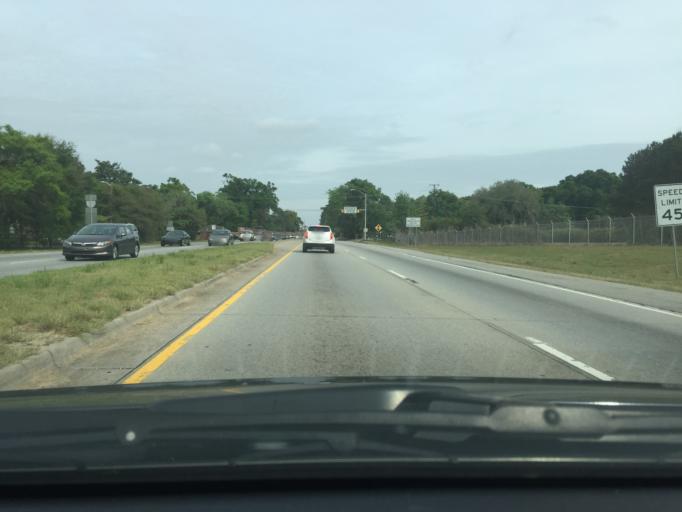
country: US
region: Georgia
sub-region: Chatham County
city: Savannah
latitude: 32.0318
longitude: -81.1212
